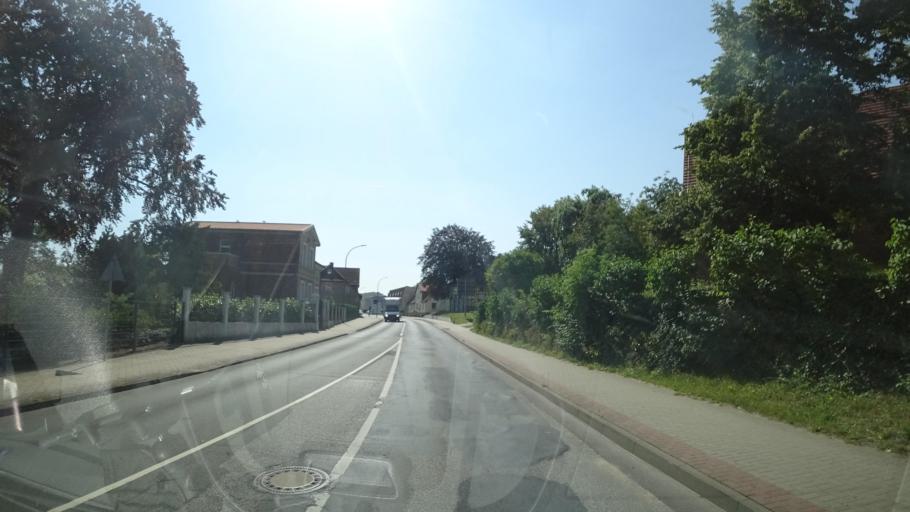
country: DE
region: Mecklenburg-Vorpommern
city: Wolgast
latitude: 54.0555
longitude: 13.7684
